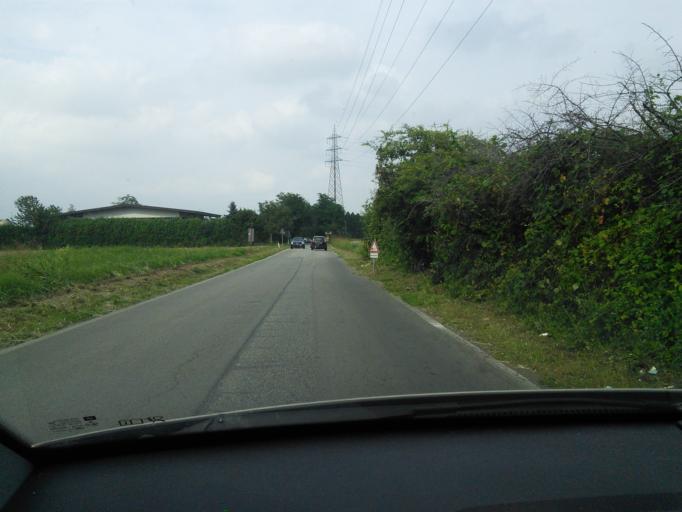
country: IT
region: Lombardy
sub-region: Citta metropolitana di Milano
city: Cerro Maggiore
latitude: 45.6058
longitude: 8.9523
